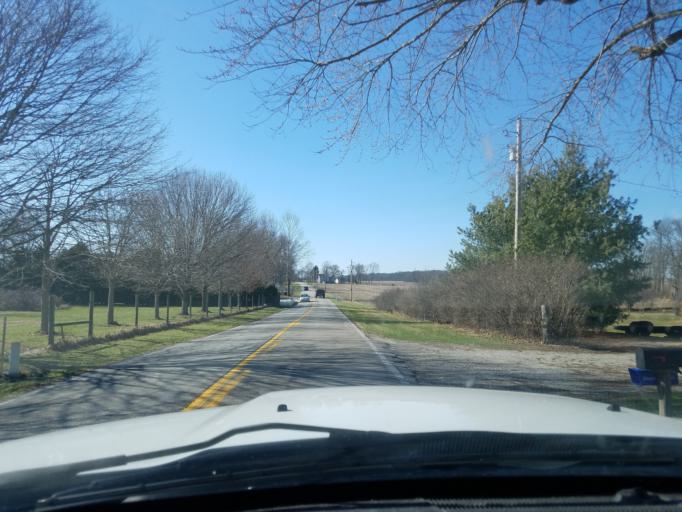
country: US
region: Indiana
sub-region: Johnson County
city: Franklin
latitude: 39.4950
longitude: -85.9832
